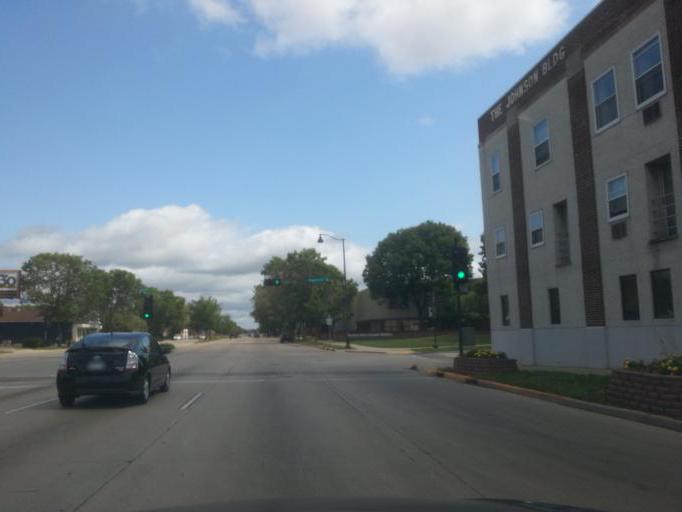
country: US
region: Wisconsin
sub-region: Dane County
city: Madison
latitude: 43.0845
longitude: -89.3701
